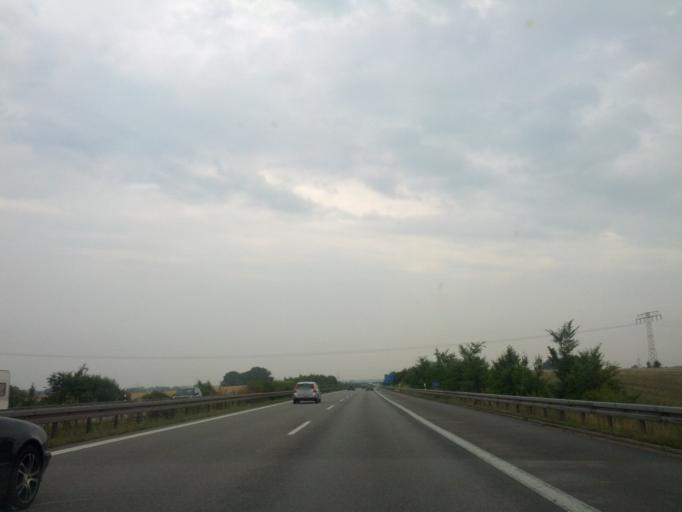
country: DE
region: Mecklenburg-Vorpommern
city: Kritzmow
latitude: 54.0196
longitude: 12.0768
